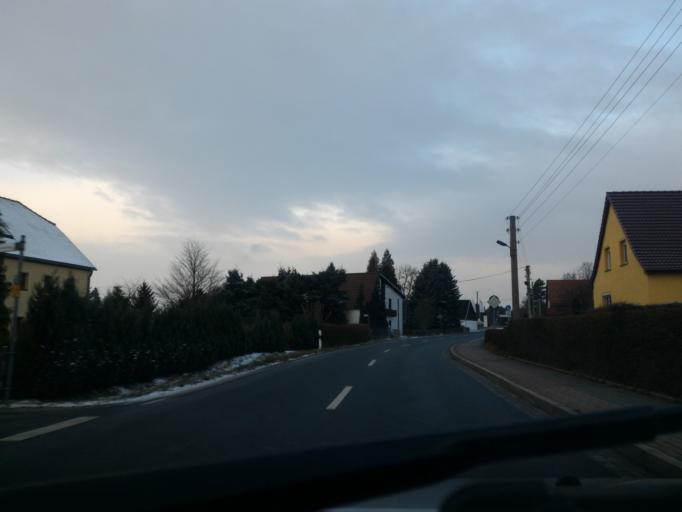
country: DE
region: Saxony
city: Leutersdorf
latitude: 50.9519
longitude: 14.6466
